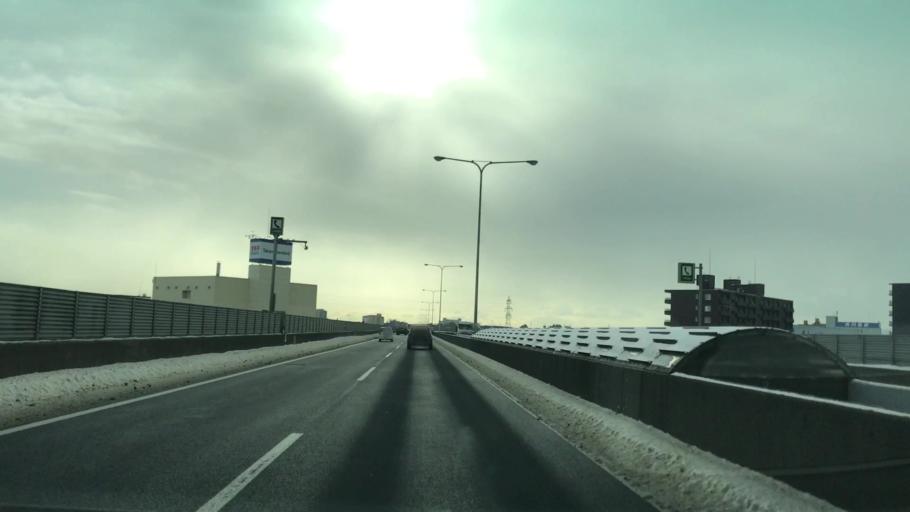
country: JP
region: Hokkaido
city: Sapporo
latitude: 43.0407
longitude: 141.4385
